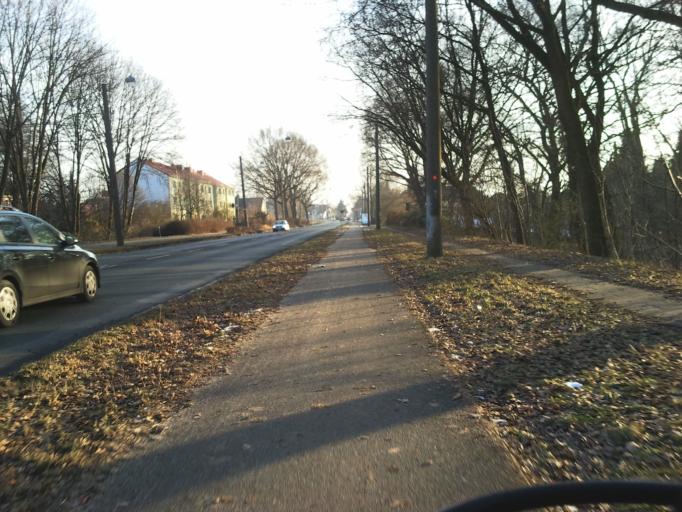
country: DE
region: Lower Saxony
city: Ritterhude
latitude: 53.1469
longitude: 8.7115
